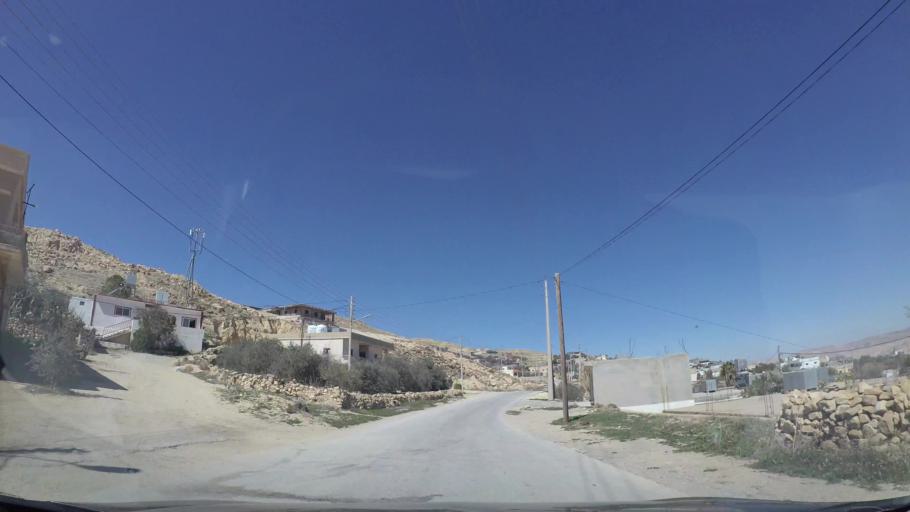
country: JO
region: Tafielah
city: At Tafilah
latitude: 30.8328
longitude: 35.5766
